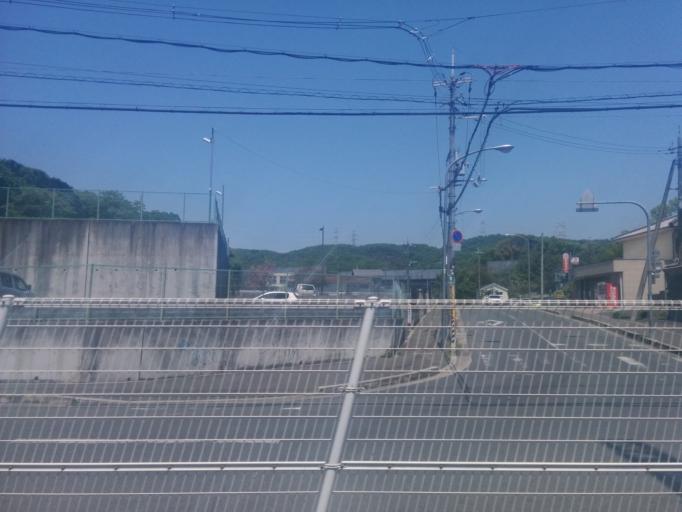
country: JP
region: Osaka
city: Kashihara
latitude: 34.5540
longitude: 135.6686
